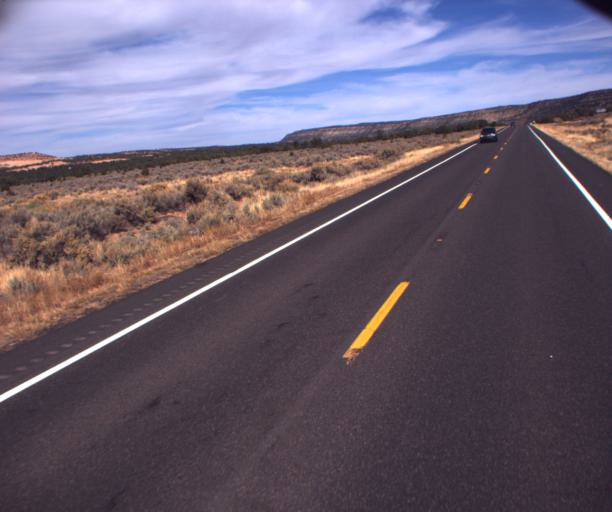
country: US
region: Arizona
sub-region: Navajo County
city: Kayenta
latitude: 36.5571
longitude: -110.5118
